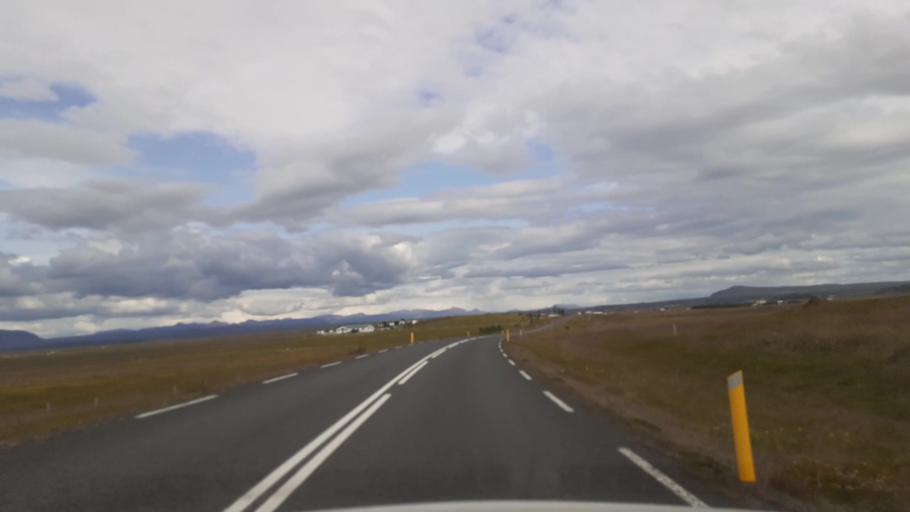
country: IS
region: South
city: Selfoss
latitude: 63.9254
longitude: -20.8516
